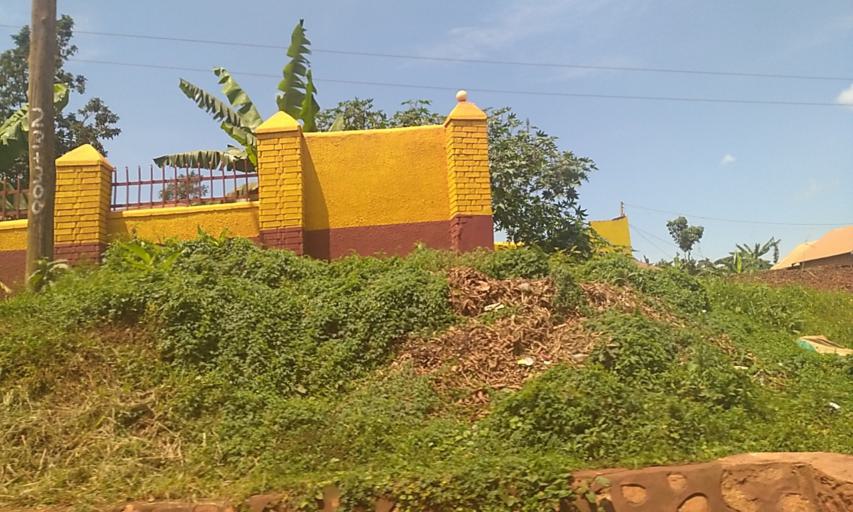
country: UG
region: Central Region
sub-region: Wakiso District
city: Wakiso
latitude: 0.4034
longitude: 32.4882
